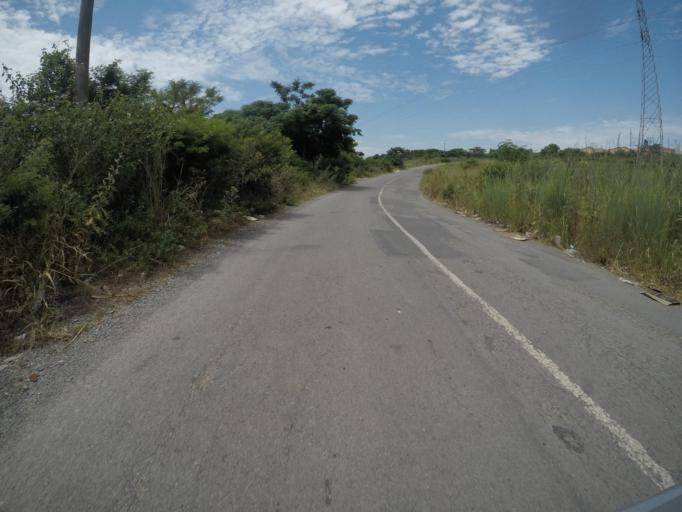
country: ZA
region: Eastern Cape
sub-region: Buffalo City Metropolitan Municipality
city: East London
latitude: -32.9744
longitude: 27.8603
